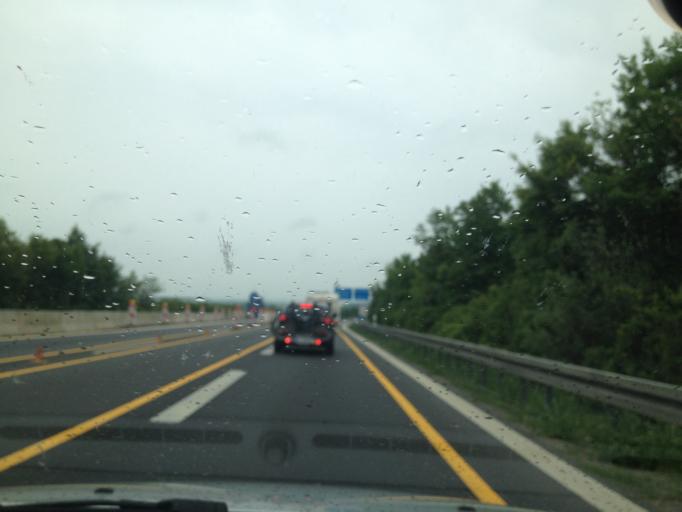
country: DE
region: Bavaria
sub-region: Regierungsbezirk Unterfranken
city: Biebelried
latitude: 49.7741
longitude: 10.0964
